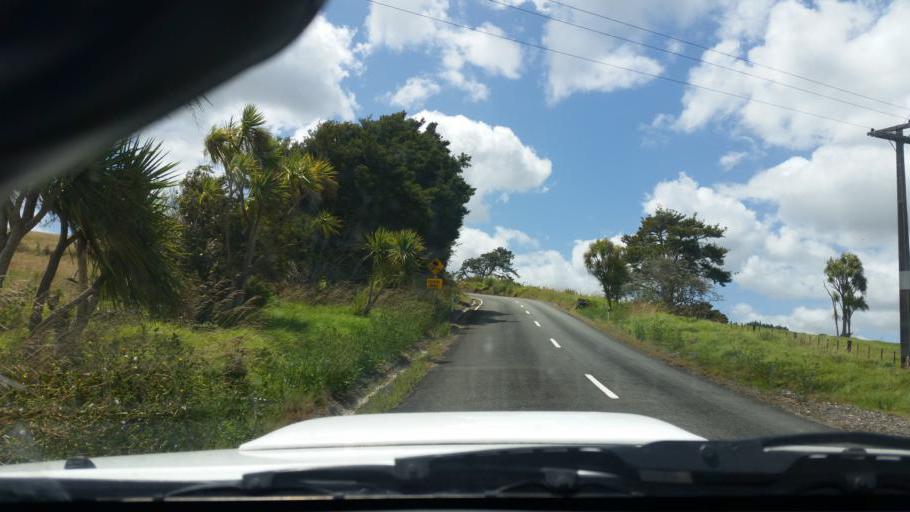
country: NZ
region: Northland
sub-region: Whangarei
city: Ruakaka
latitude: -36.0973
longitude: 174.2319
